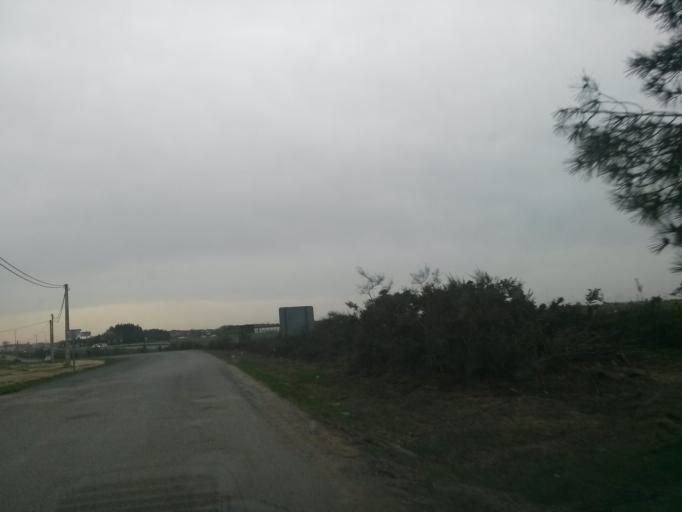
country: ES
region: Galicia
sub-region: Provincia de Lugo
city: Lugo
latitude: 43.0334
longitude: -7.5491
